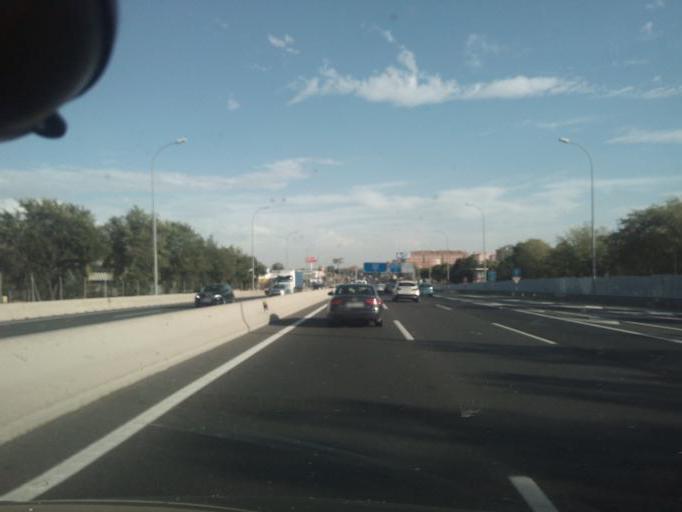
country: ES
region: Madrid
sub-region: Provincia de Madrid
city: Valdemoro
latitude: 40.2021
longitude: -3.6783
